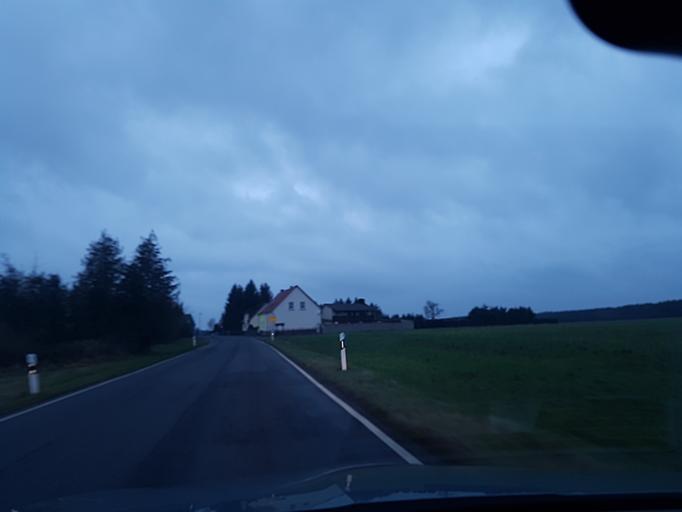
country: DE
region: Brandenburg
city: Schilda
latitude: 51.6036
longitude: 13.4054
